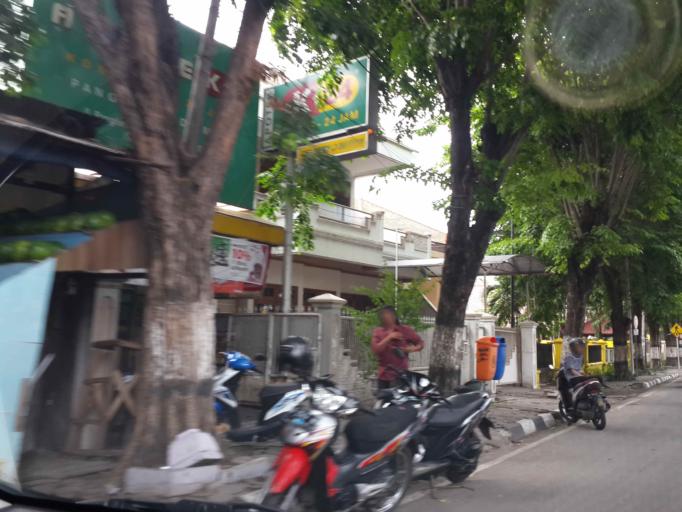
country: ID
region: East Java
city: Gresik
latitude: -7.1694
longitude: 112.6541
